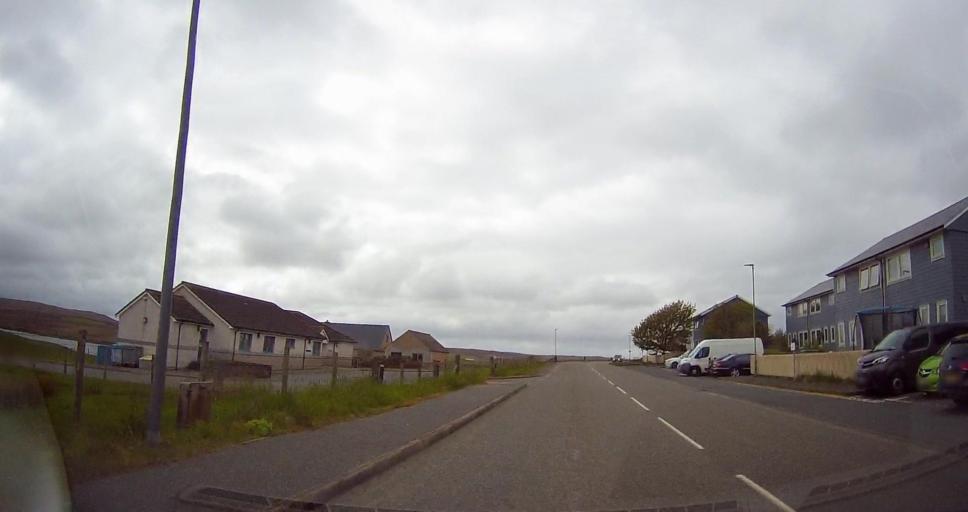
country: GB
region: Scotland
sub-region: Shetland Islands
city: Lerwick
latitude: 60.2529
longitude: -1.3975
